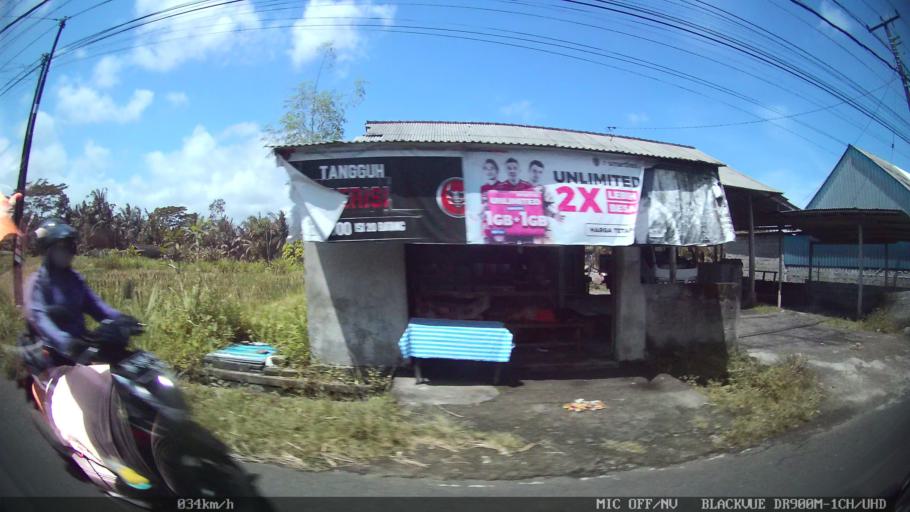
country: ID
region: Bali
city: Banjar Kelodan
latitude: -8.5318
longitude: 115.3356
